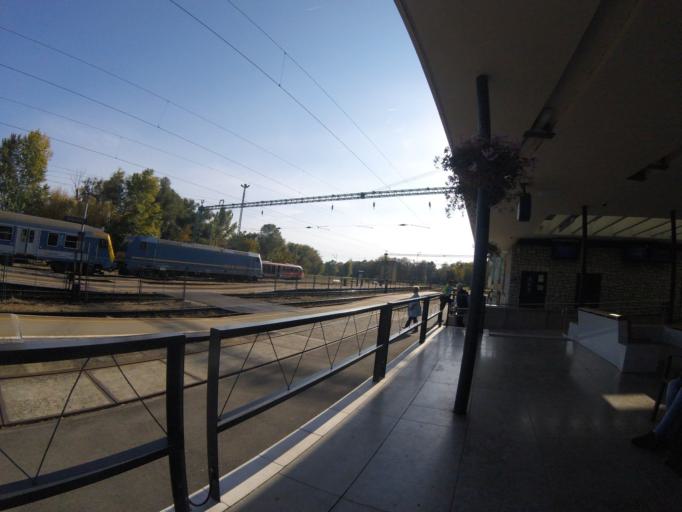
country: HU
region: Zala
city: Keszthely
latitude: 46.7578
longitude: 17.2470
